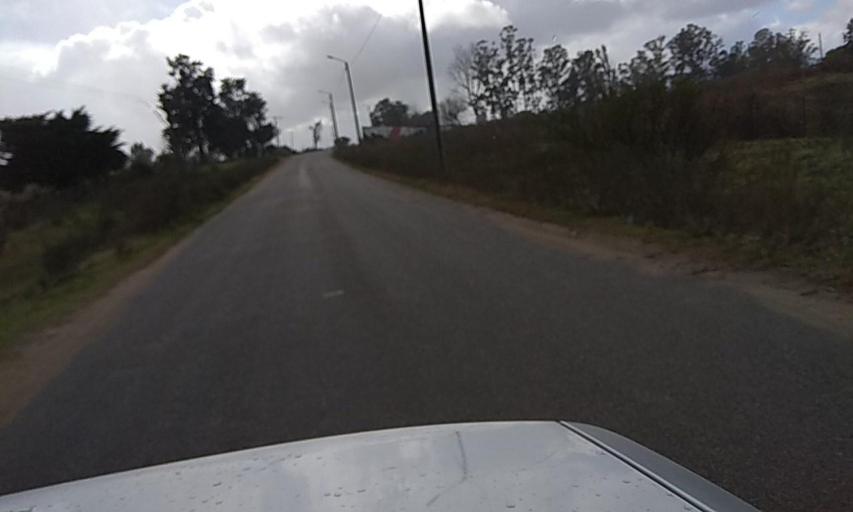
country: UY
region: Florida
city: Florida
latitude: -34.1110
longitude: -56.2263
